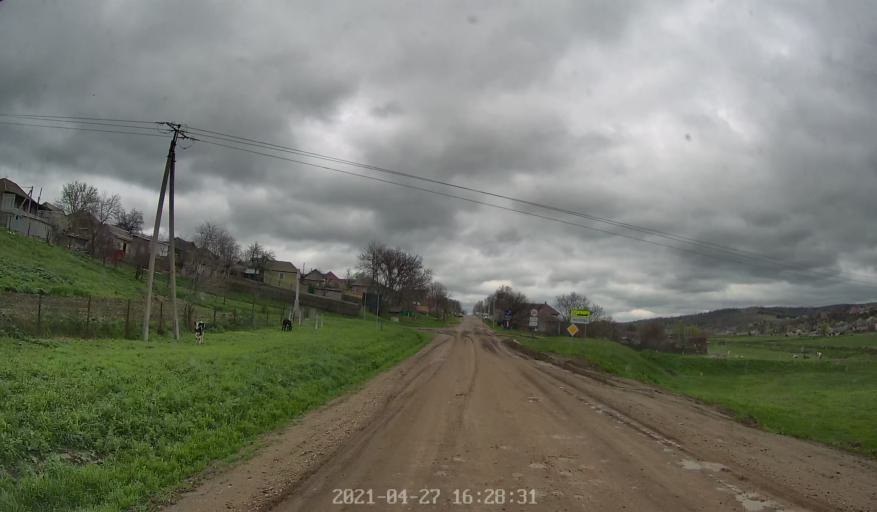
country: MD
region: Chisinau
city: Singera
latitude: 46.9714
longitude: 29.0428
